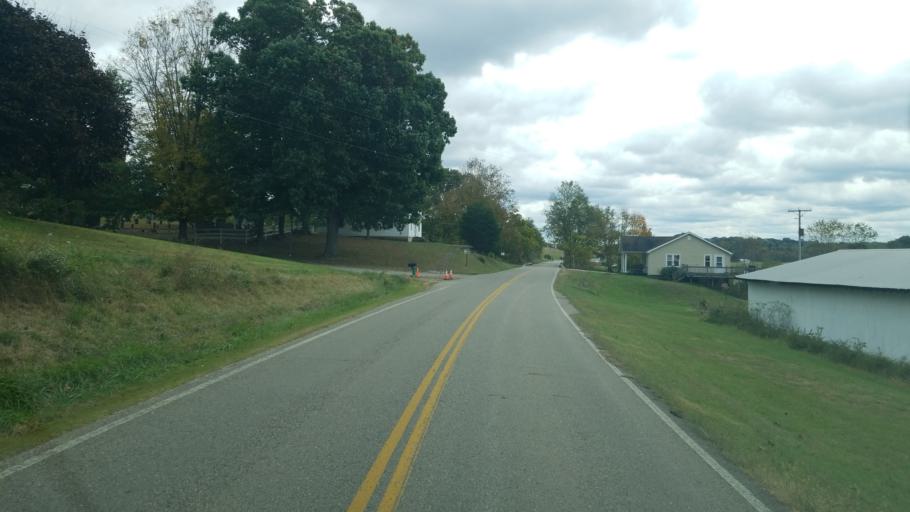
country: US
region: Ohio
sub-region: Jackson County
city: Jackson
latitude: 39.1411
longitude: -82.6540
